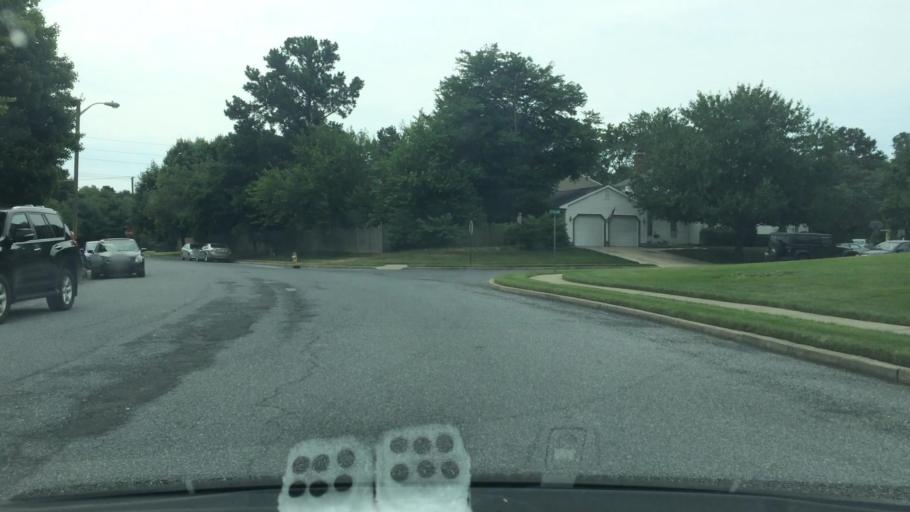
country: US
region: New Jersey
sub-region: Gloucester County
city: Turnersville
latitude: 39.7751
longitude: -75.0666
